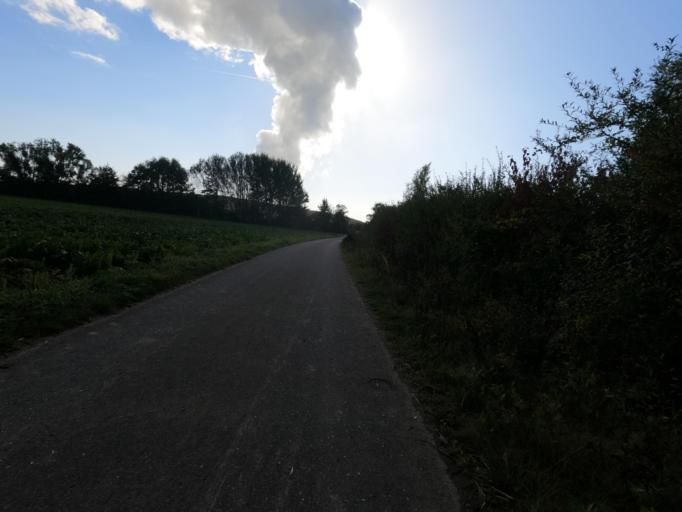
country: DE
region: North Rhine-Westphalia
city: Neu-Pattern
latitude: 50.8599
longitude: 6.3050
